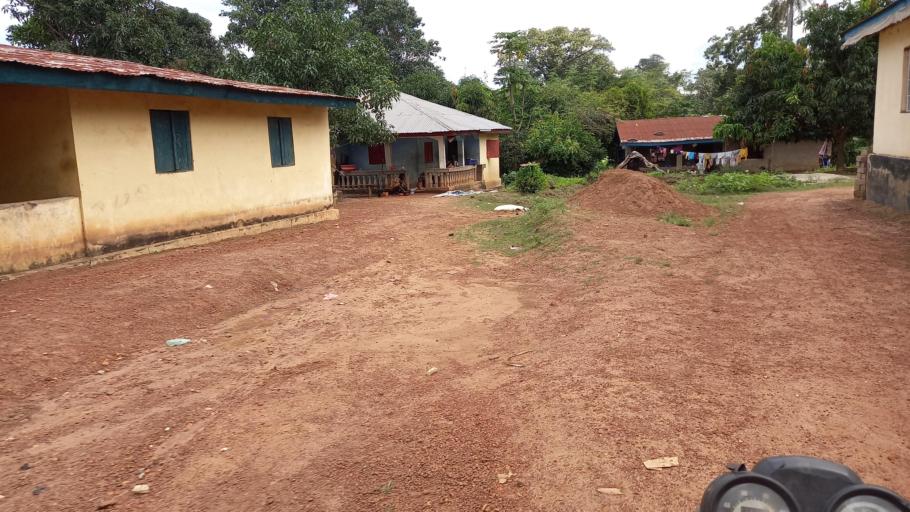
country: SL
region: Northern Province
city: Kamakwie
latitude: 9.5030
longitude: -12.2406
